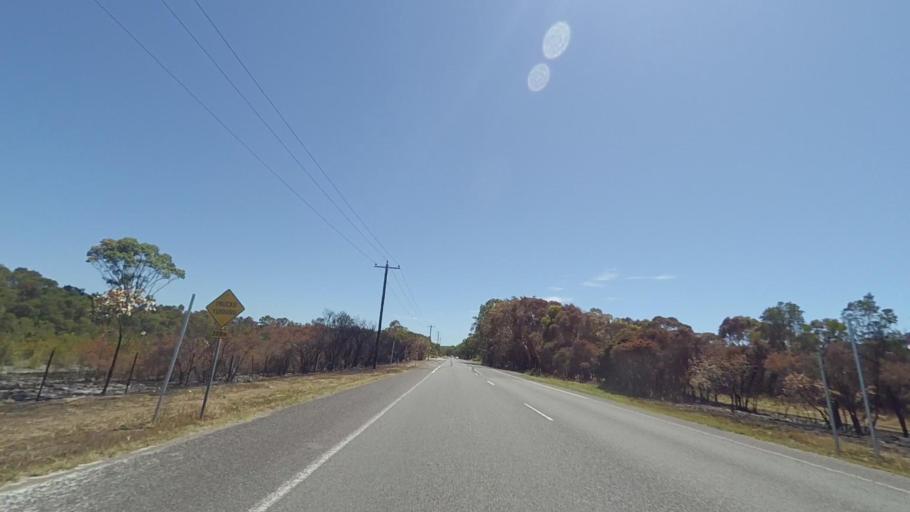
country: AU
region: New South Wales
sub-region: Port Stephens Shire
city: Medowie
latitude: -32.7856
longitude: 151.8567
